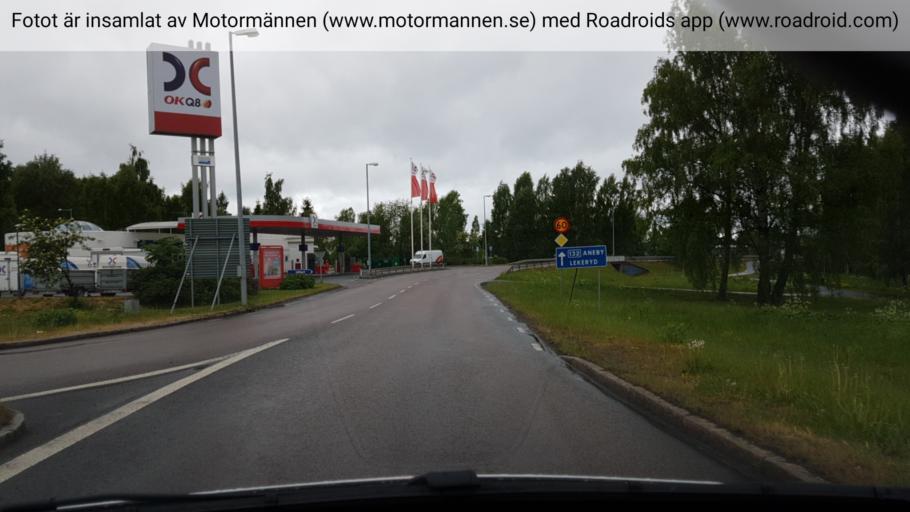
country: SE
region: Joenkoeping
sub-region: Jonkopings Kommun
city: Huskvarna
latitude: 57.7888
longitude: 14.2665
